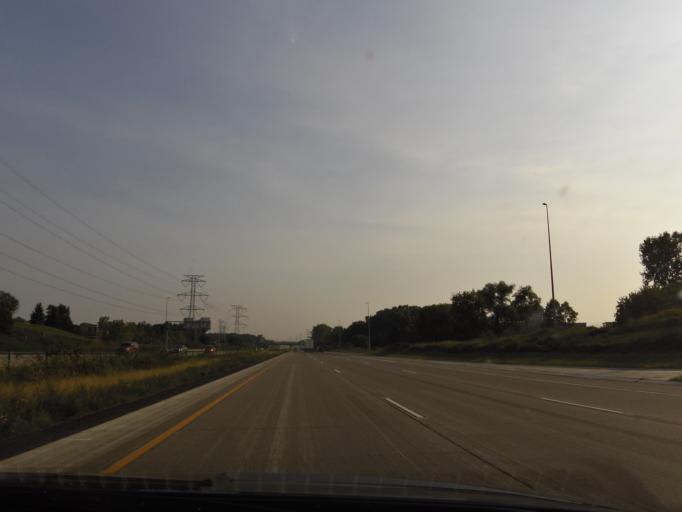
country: US
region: Minnesota
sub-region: Hennepin County
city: Plymouth
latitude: 44.9803
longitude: -93.4601
